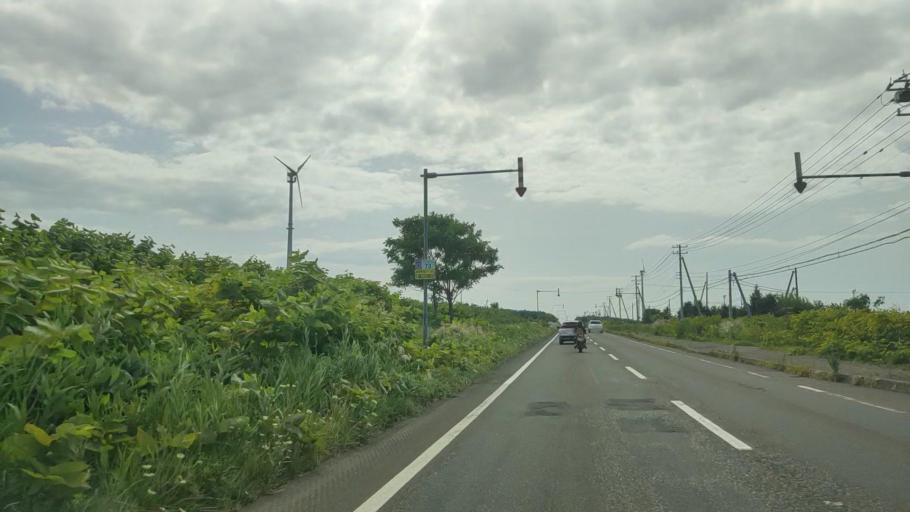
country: JP
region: Hokkaido
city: Rumoi
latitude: 44.4007
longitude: 141.7239
